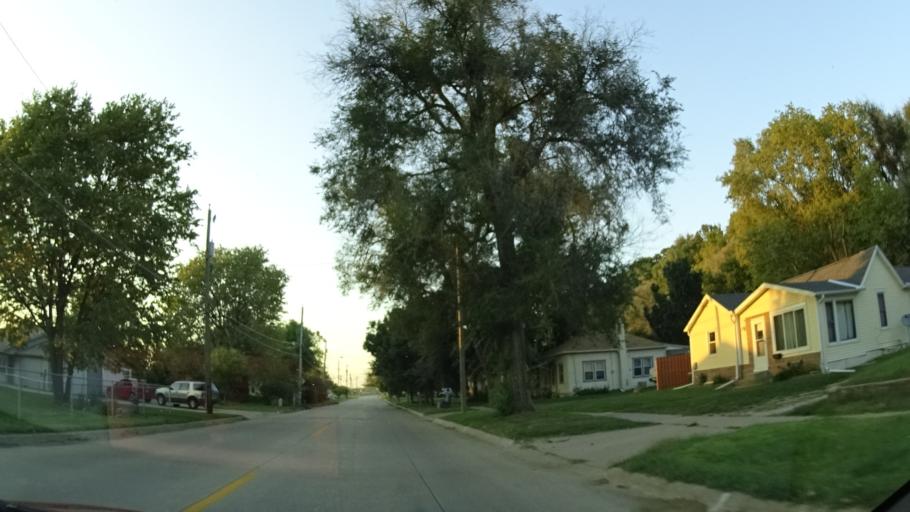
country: US
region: Iowa
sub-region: Pottawattamie County
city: Council Bluffs
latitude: 41.2725
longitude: -95.8575
